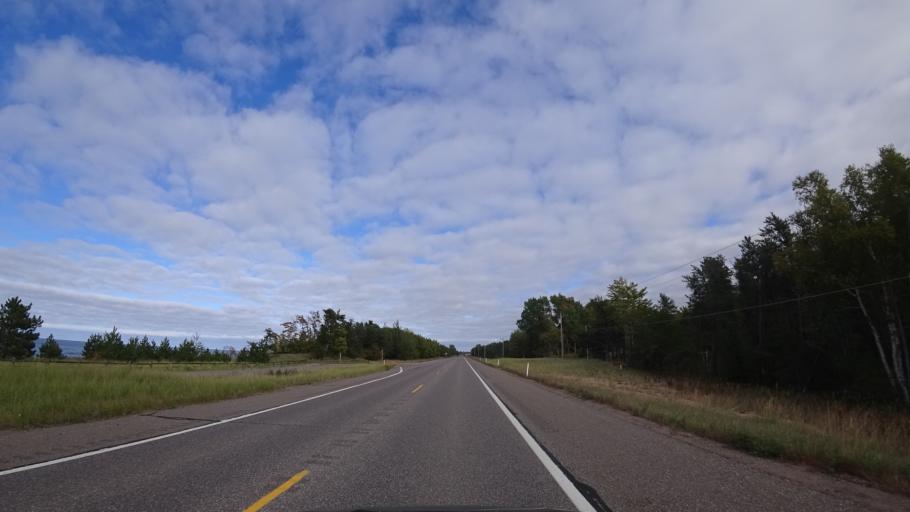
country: US
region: Michigan
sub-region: Marquette County
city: Harvey
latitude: 46.4896
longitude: -87.2074
